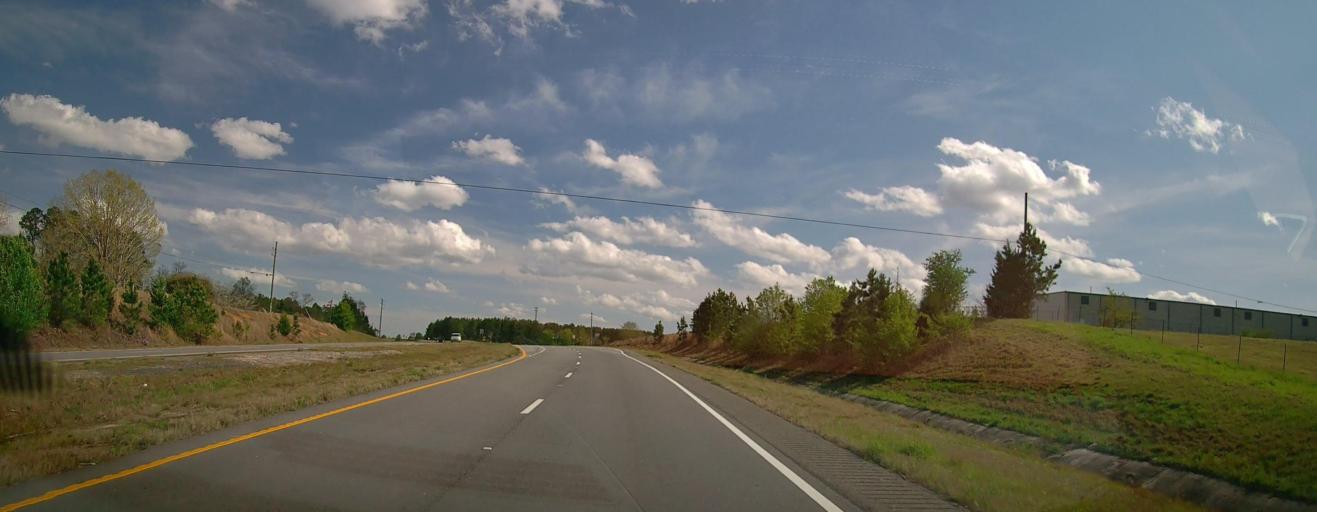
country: US
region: Georgia
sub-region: Baldwin County
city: Hardwick
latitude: 33.0037
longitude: -83.2207
